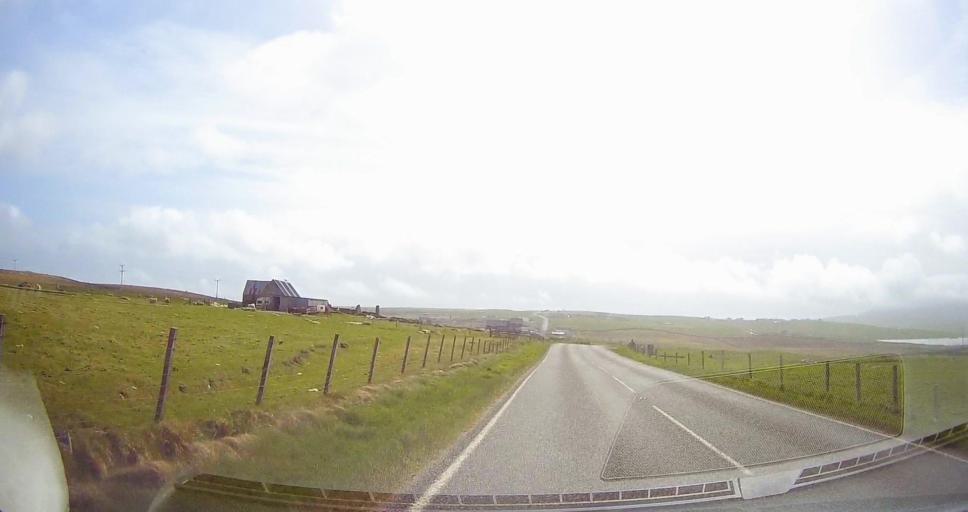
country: GB
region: Scotland
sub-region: Shetland Islands
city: Sandwick
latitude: 59.9326
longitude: -1.2944
